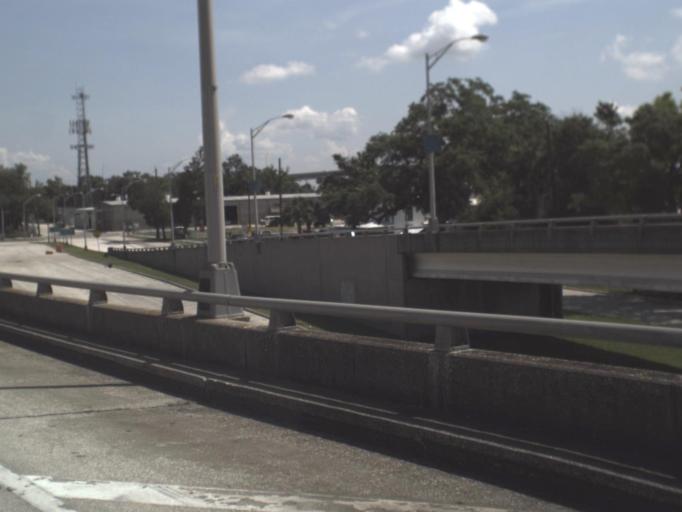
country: US
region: Florida
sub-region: Duval County
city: Jacksonville
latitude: 30.3227
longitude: -81.6345
